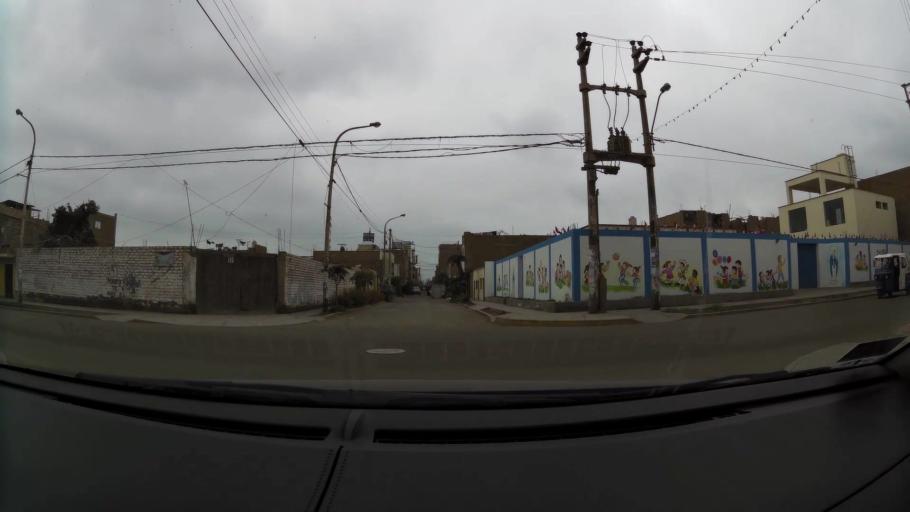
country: PE
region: Lima
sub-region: Provincia de Huaral
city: Huaral
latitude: -11.5011
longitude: -77.2138
